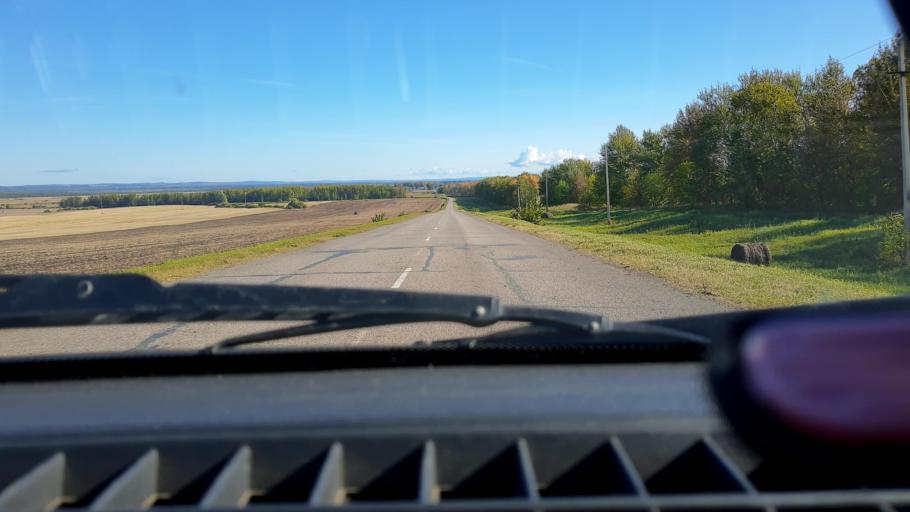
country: RU
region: Bashkortostan
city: Kushnarenkovo
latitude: 55.0770
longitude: 55.4636
